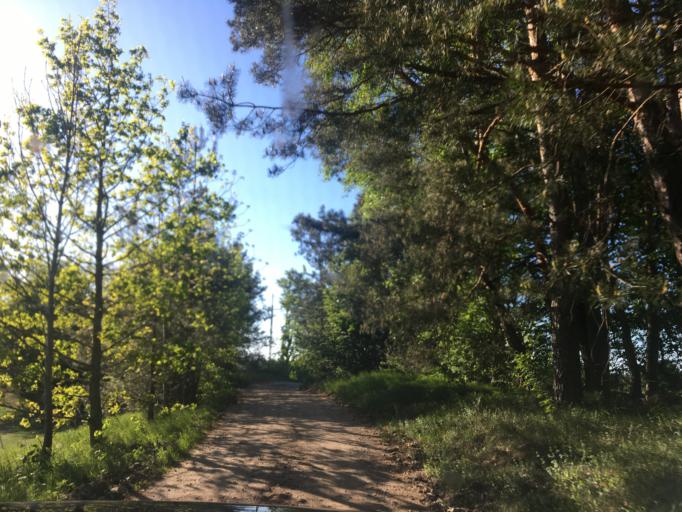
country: PL
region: Warmian-Masurian Voivodeship
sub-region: Powiat piski
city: Ruciane-Nida
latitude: 53.6570
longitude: 21.4830
